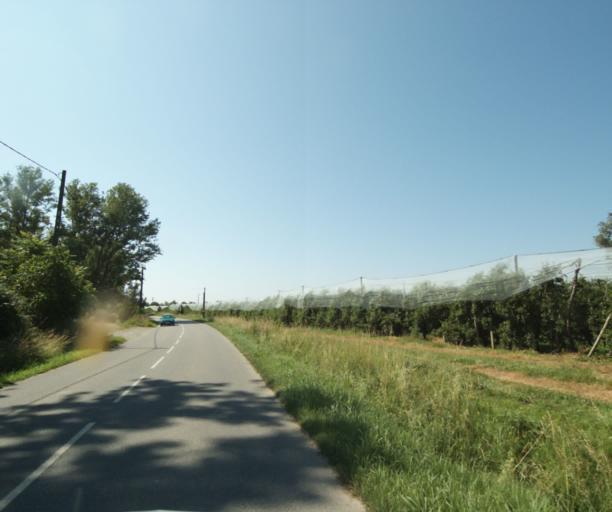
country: FR
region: Midi-Pyrenees
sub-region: Departement du Tarn-et-Garonne
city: Montbeton
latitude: 44.0353
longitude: 1.2989
